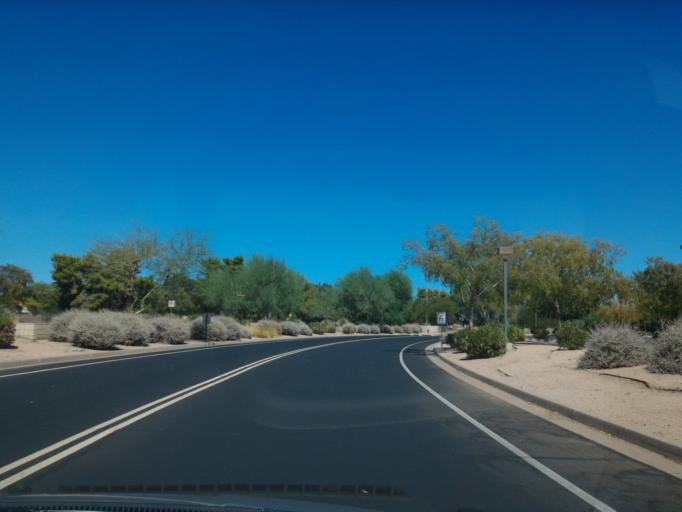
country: US
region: Arizona
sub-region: Maricopa County
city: Guadalupe
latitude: 33.3122
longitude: -111.9355
